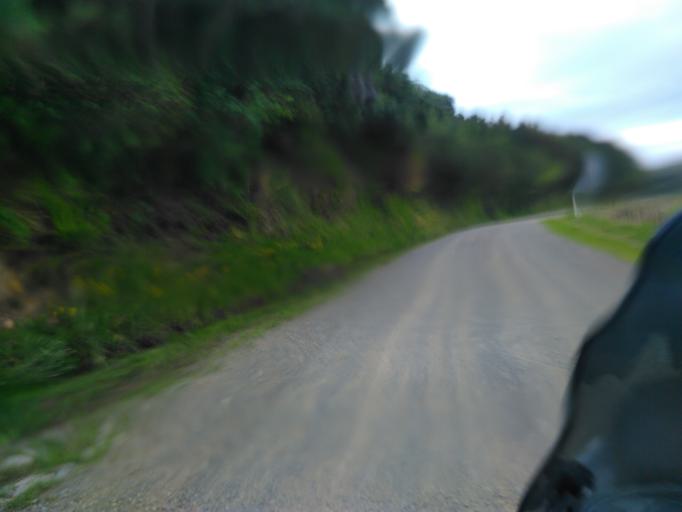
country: NZ
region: Bay of Plenty
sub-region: Opotiki District
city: Opotiki
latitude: -38.0232
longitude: 177.4356
